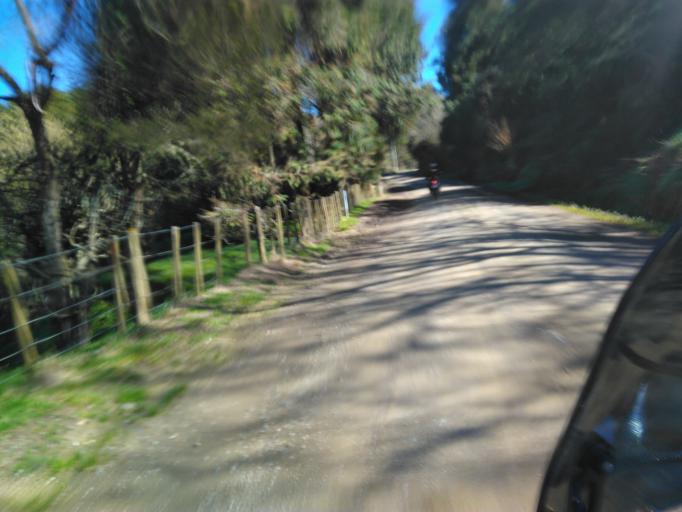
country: NZ
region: Bay of Plenty
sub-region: Opotiki District
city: Opotiki
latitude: -38.2949
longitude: 177.5515
